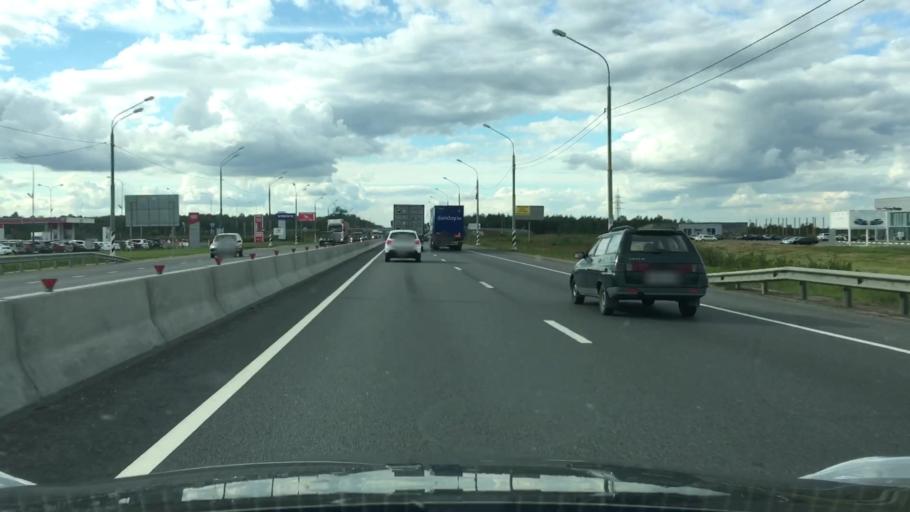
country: RU
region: Tverskaya
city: Tver
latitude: 56.7897
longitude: 35.9077
